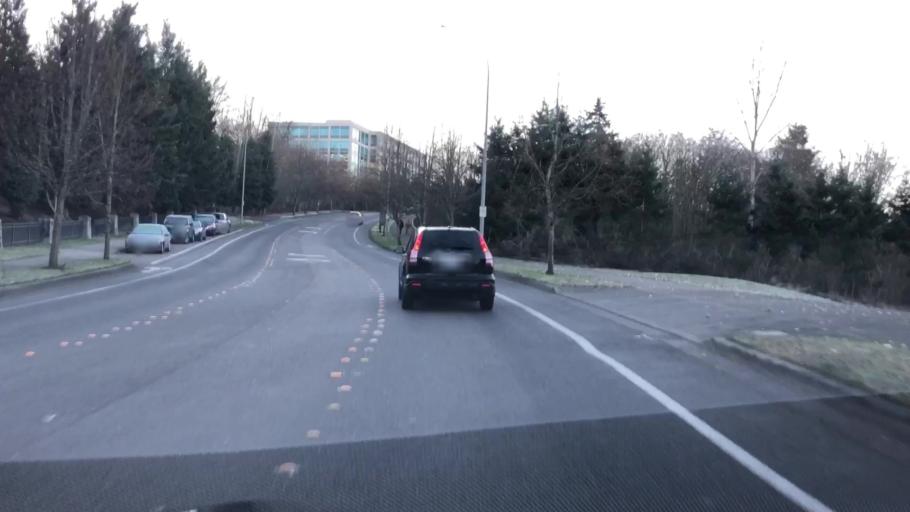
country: US
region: Washington
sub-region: King County
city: Eastgate
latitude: 47.5858
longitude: -122.1558
